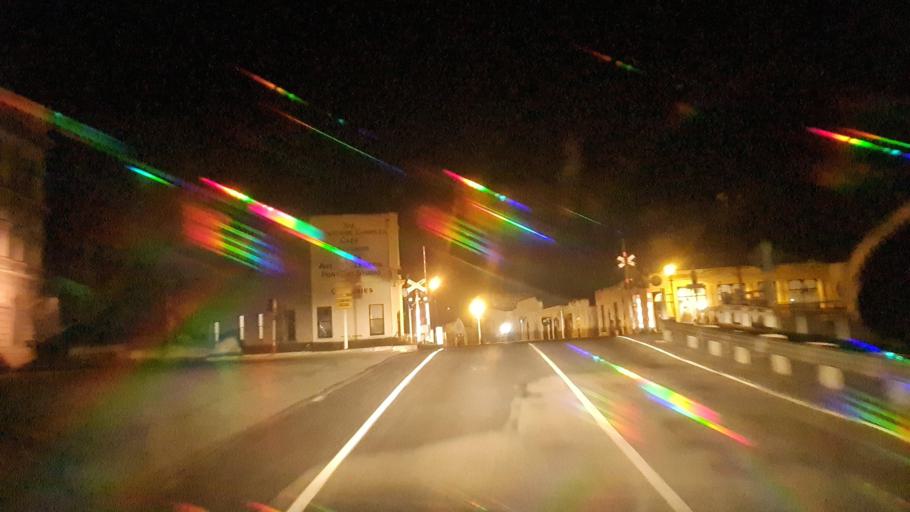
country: NZ
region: Otago
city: Oamaru
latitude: -45.1020
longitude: 170.9704
